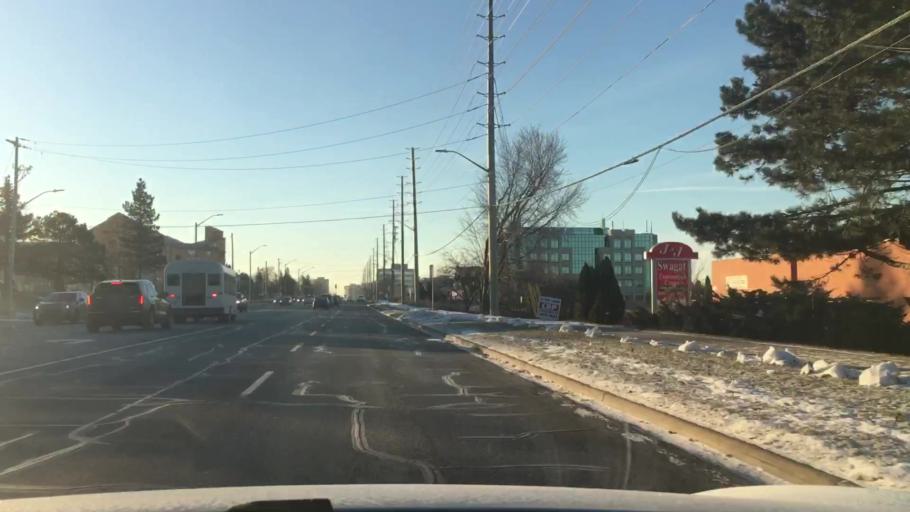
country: CA
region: Ontario
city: Markham
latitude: 43.8307
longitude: -79.3274
